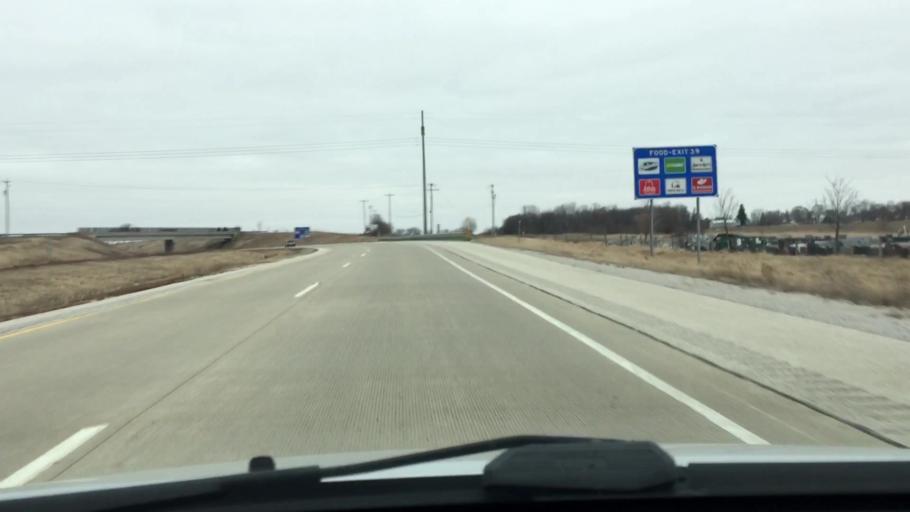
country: US
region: Wisconsin
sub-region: Jefferson County
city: Watertown
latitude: 43.1479
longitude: -88.7345
